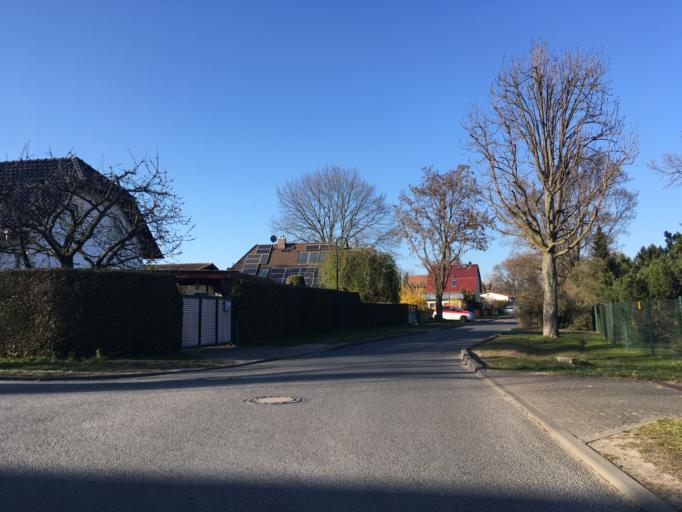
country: DE
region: Berlin
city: Buch
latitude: 52.6372
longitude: 13.5234
